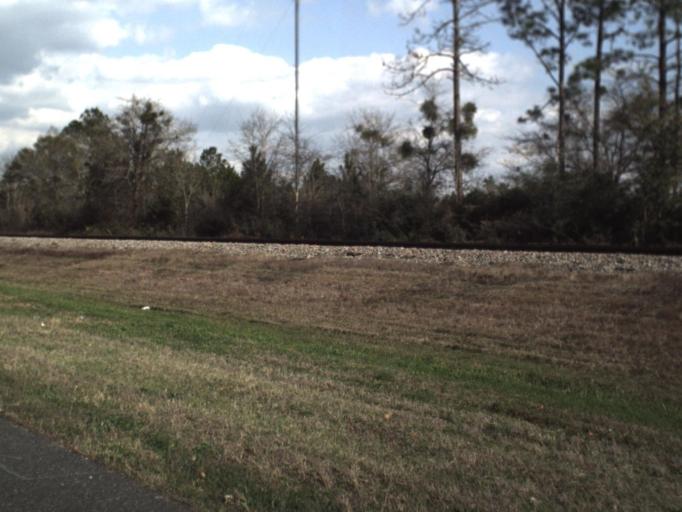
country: US
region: Florida
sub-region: Bay County
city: Hiland Park
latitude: 30.2681
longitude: -85.5296
